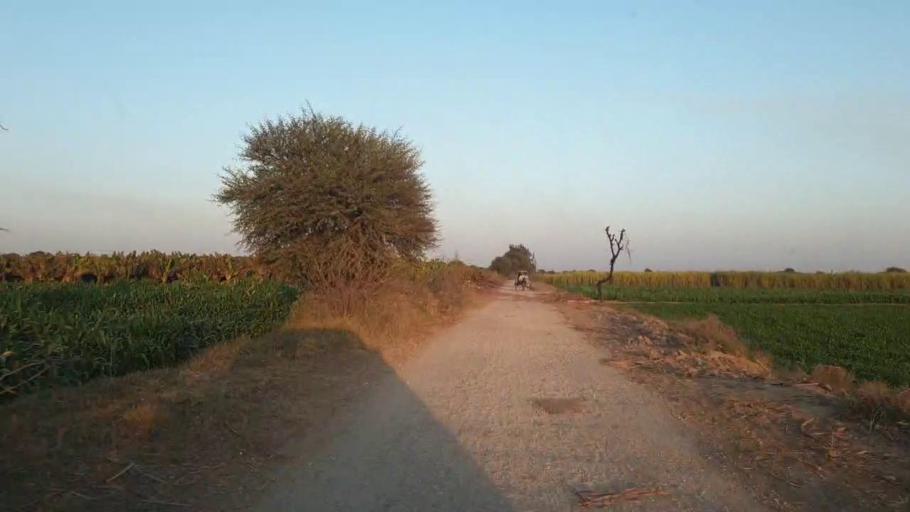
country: PK
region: Sindh
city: Tando Allahyar
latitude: 25.3634
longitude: 68.7352
